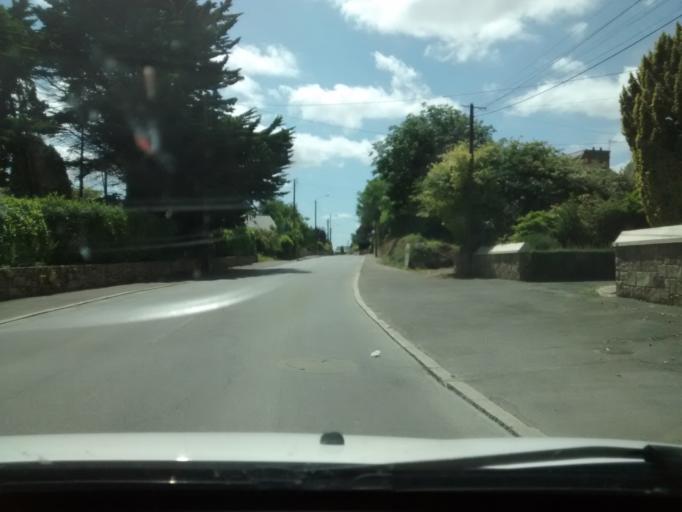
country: FR
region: Brittany
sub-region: Departement des Cotes-d'Armor
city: Penvenan
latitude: 48.8187
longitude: -3.2982
